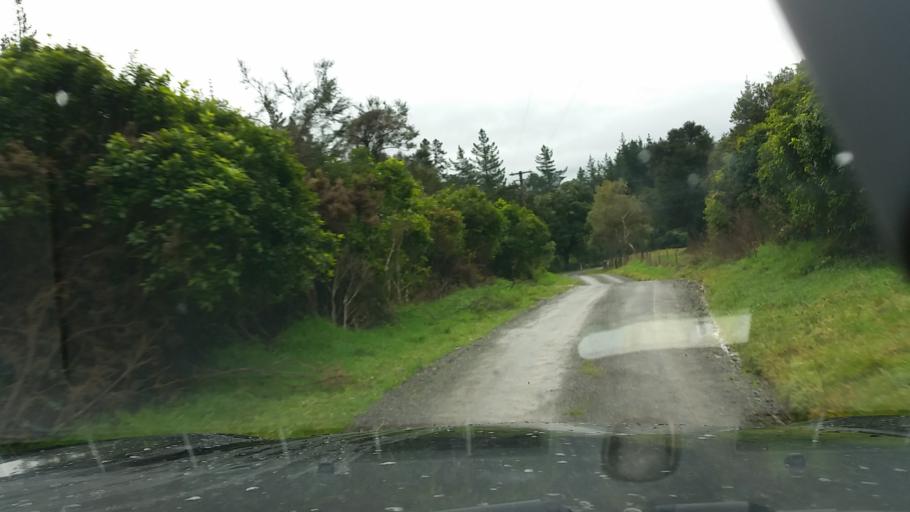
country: NZ
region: Marlborough
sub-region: Marlborough District
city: Picton
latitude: -41.2899
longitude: 174.0398
